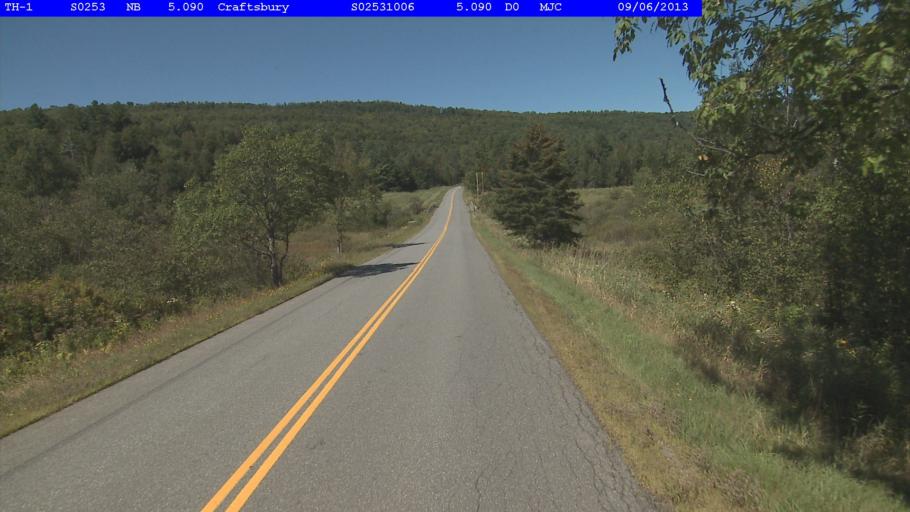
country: US
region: Vermont
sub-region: Caledonia County
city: Hardwick
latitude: 44.6764
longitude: -72.3992
